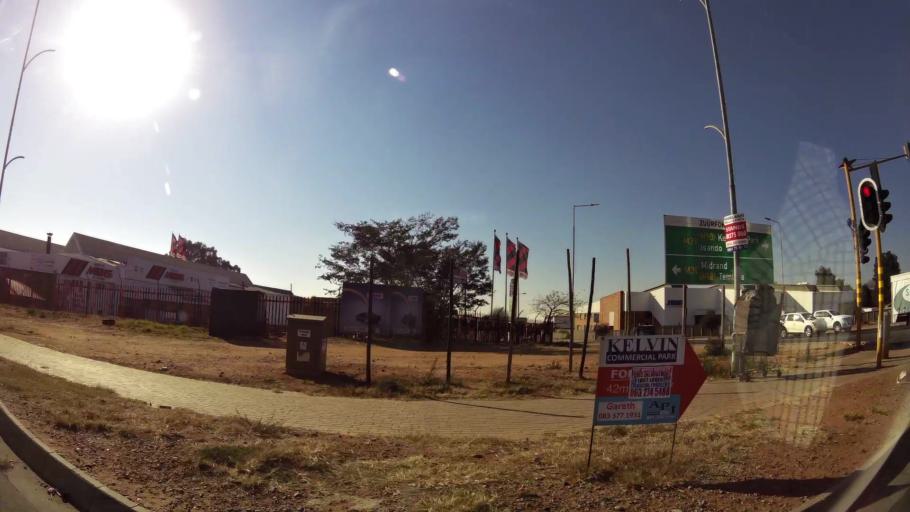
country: ZA
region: Gauteng
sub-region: City of Johannesburg Metropolitan Municipality
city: Modderfontein
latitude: -26.0689
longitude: 28.1861
